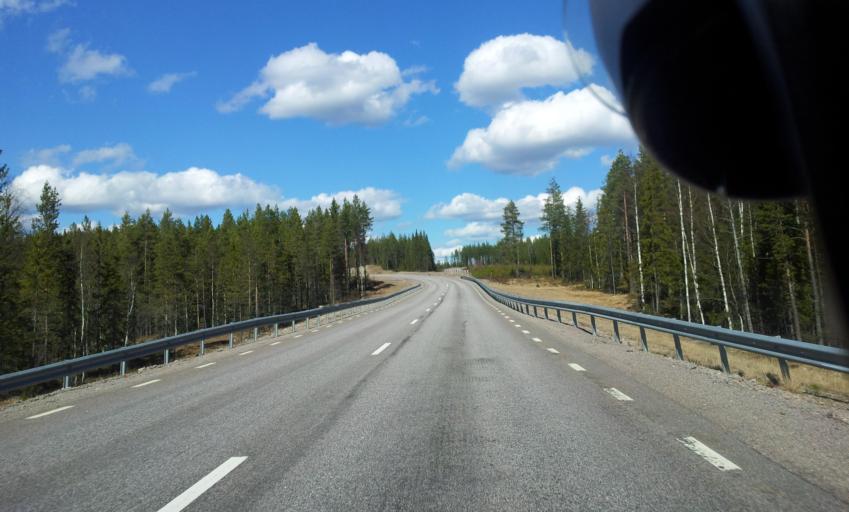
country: SE
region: Gaevleborg
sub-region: Bollnas Kommun
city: Vittsjo
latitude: 61.1199
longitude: 15.8656
